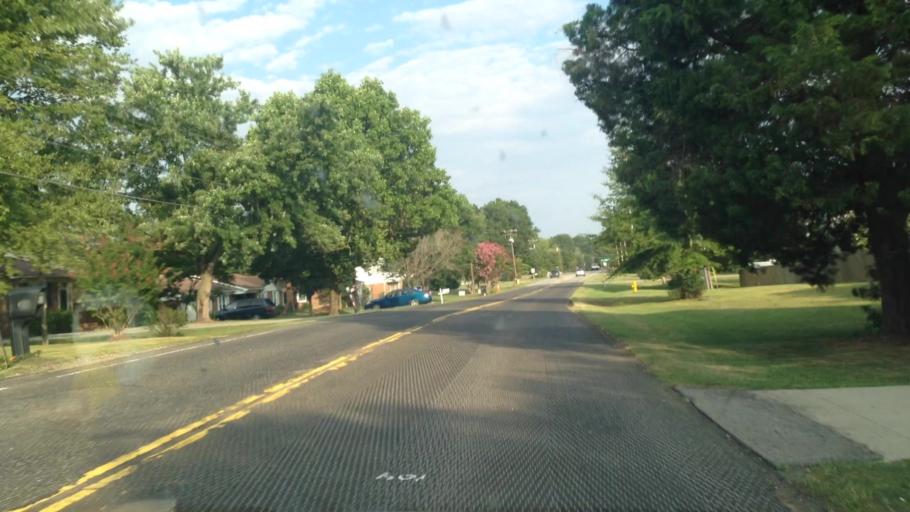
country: US
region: North Carolina
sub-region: Forsyth County
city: Kernersville
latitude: 36.0443
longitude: -80.0560
